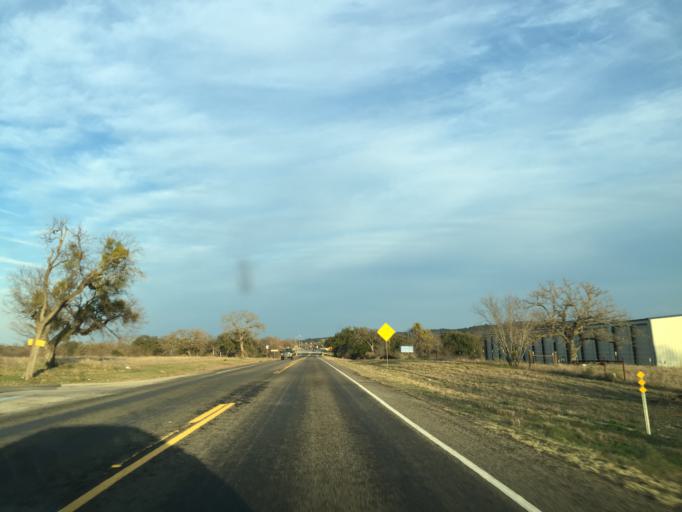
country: US
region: Texas
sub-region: Llano County
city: Buchanan Dam
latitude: 30.7331
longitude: -98.4716
